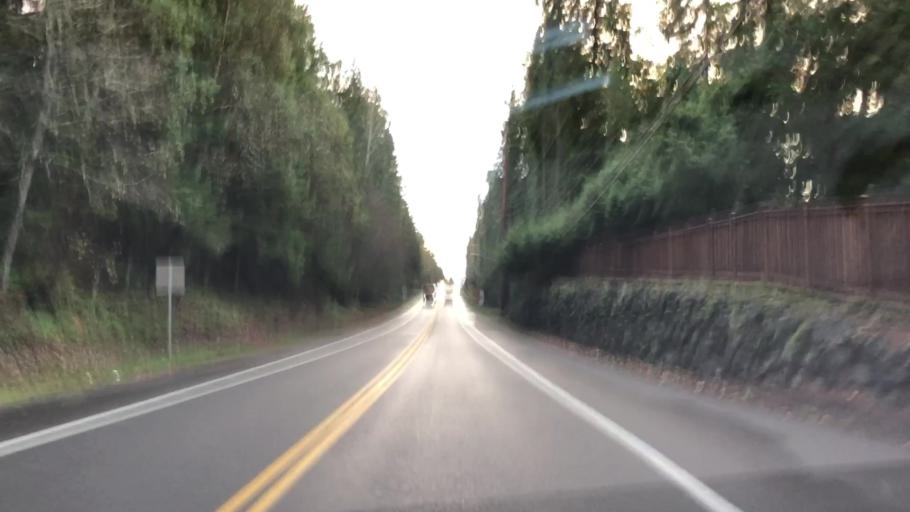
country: US
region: Washington
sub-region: King County
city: Sammamish
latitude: 47.6399
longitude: -122.0533
